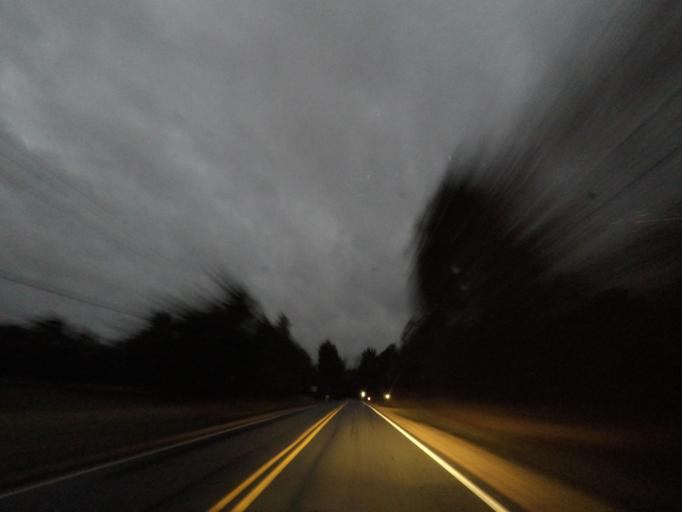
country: US
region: North Carolina
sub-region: Orange County
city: Hillsborough
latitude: 36.0674
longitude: -78.9886
